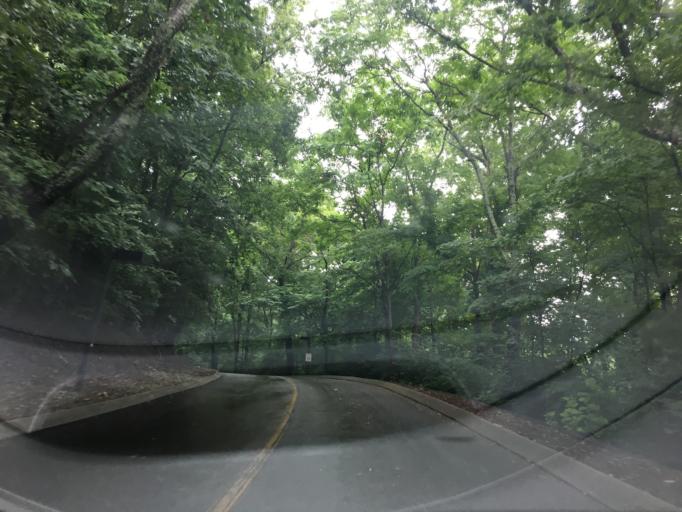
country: US
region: Tennessee
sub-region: Davidson County
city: Belle Meade
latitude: 36.0722
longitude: -86.8969
